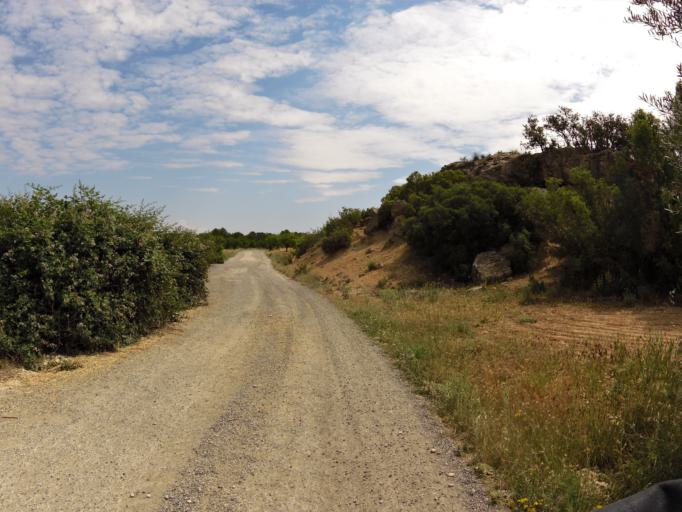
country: ES
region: Castille-La Mancha
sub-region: Provincia de Albacete
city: Casas Ibanez
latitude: 39.3537
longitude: -1.4778
